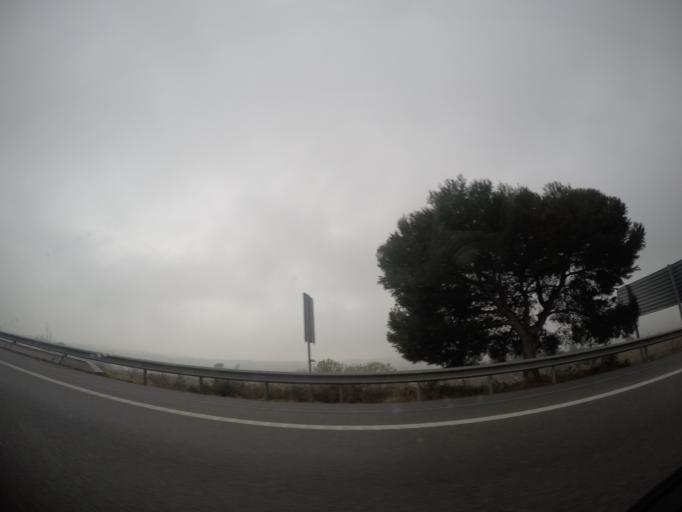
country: ES
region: Catalonia
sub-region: Provincia de Barcelona
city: Sant Sadurni d'Anoia
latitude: 41.4116
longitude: 1.7834
